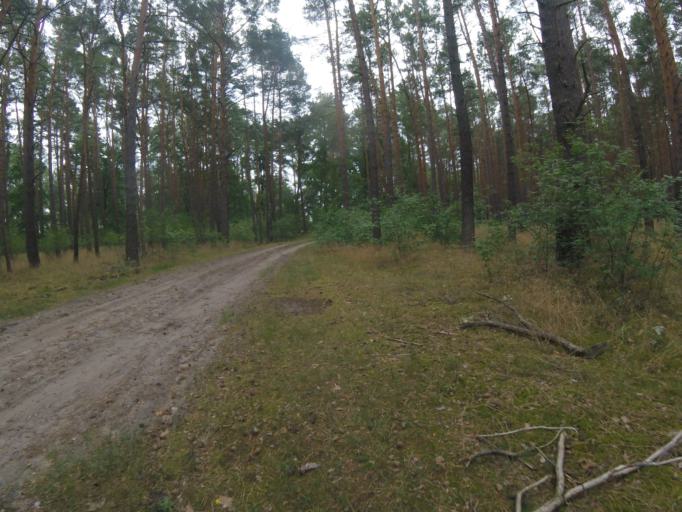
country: DE
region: Brandenburg
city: Bestensee
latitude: 52.2606
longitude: 13.7044
